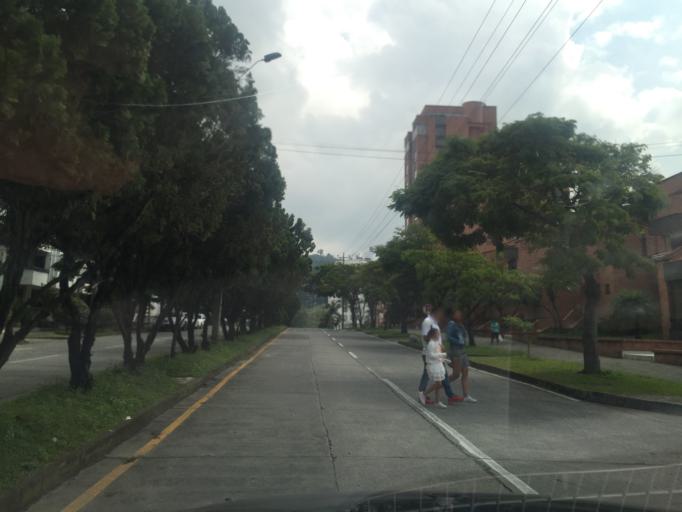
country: CO
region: Risaralda
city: Pereira
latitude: 4.8042
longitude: -75.6861
